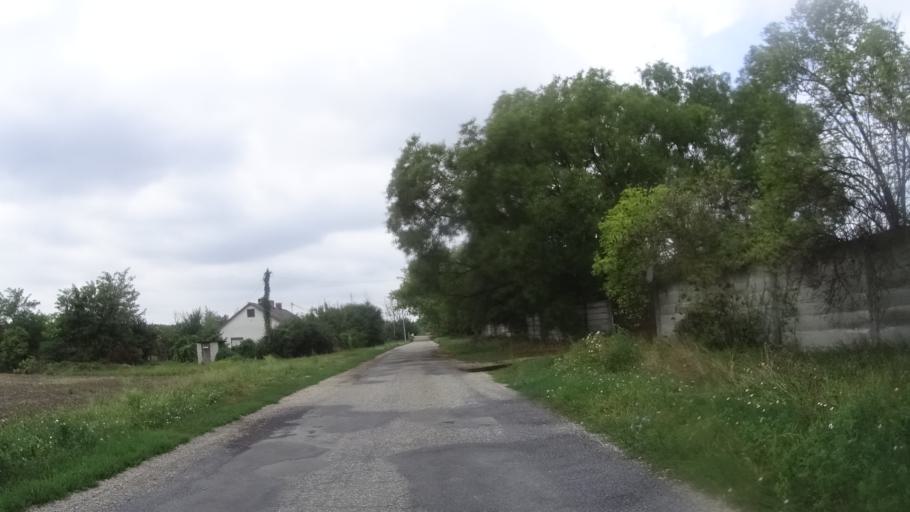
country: HU
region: Komarom-Esztergom
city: Acs
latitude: 47.7592
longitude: 17.9491
